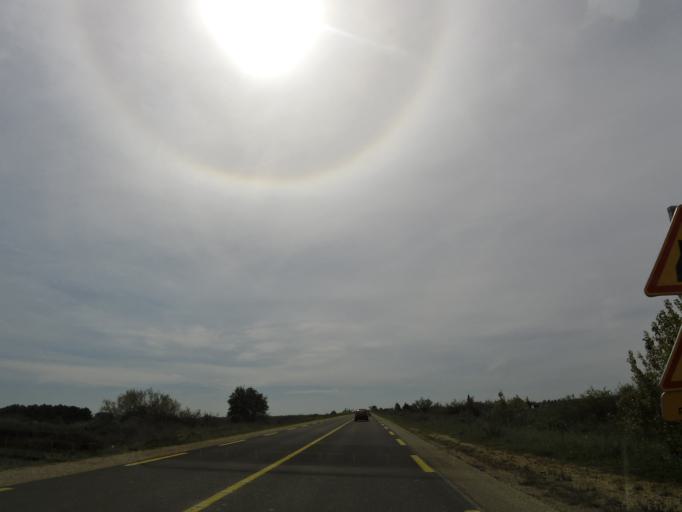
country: FR
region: Languedoc-Roussillon
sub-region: Departement de l'Herault
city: La Grande-Motte
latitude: 43.5896
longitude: 4.1049
